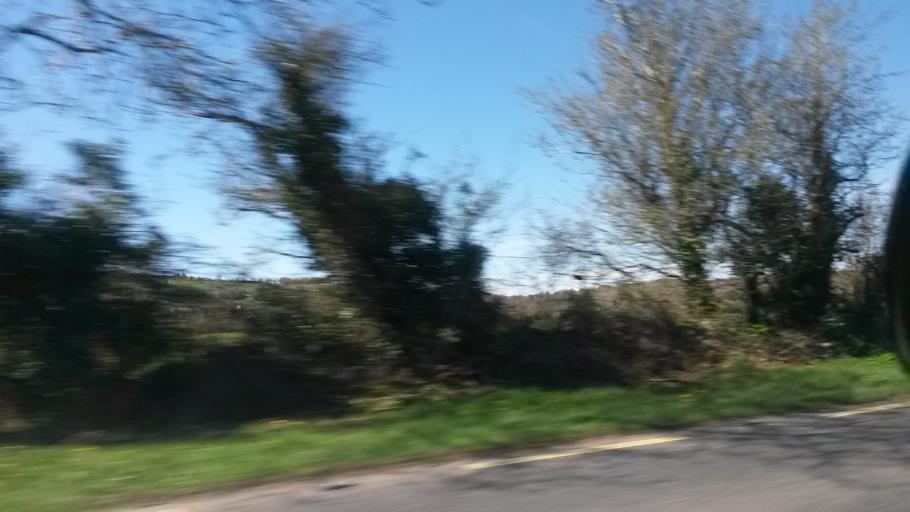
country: IE
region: Munster
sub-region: County Cork
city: Macroom
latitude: 51.9117
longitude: -9.0501
